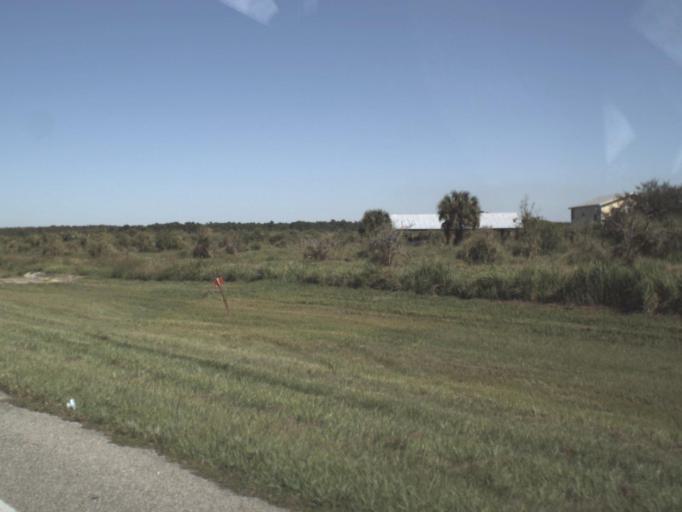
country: US
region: Florida
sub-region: Hendry County
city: LaBelle
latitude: 26.7328
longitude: -81.4772
